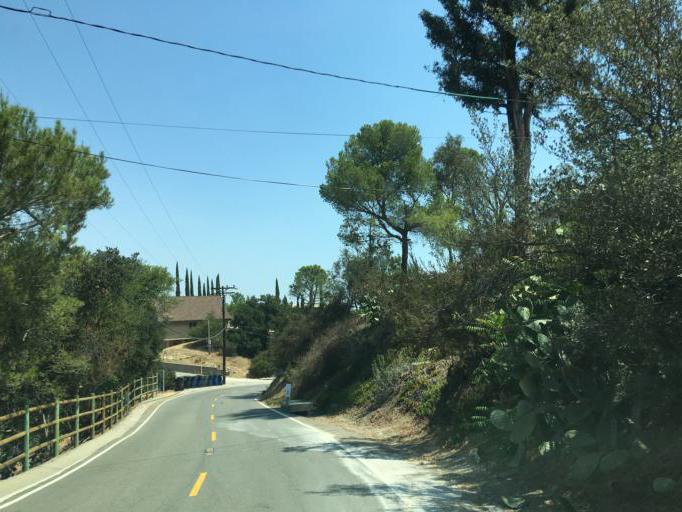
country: US
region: California
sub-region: Los Angeles County
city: Topanga
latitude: 34.0690
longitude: -118.6094
